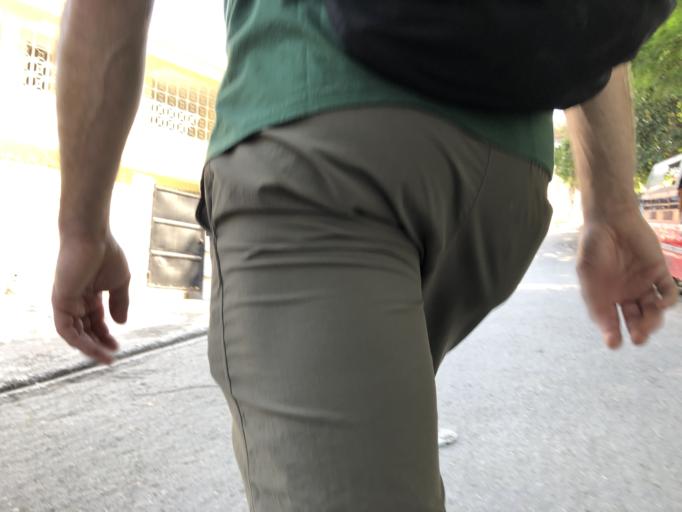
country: HT
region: Ouest
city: Port-au-Prince
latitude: 18.5251
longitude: -72.3191
